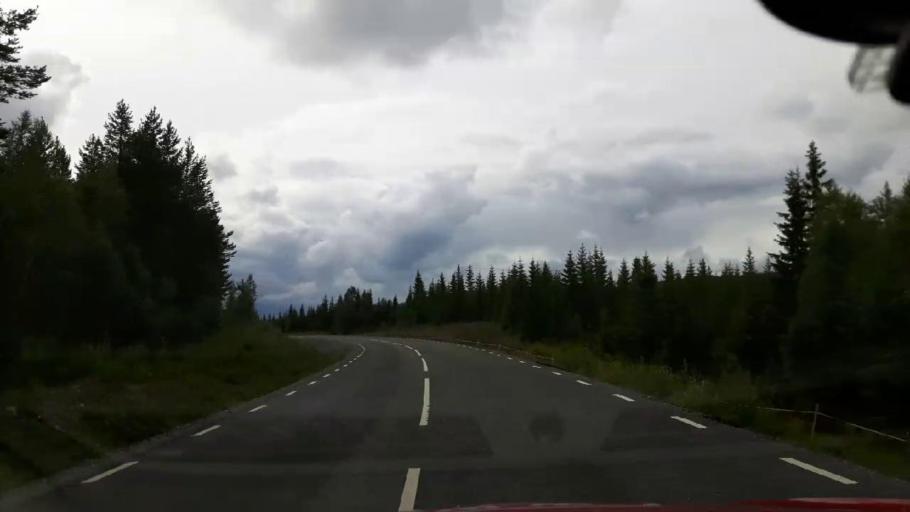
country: NO
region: Nord-Trondelag
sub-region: Lierne
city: Sandvika
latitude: 64.6274
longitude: 14.1242
